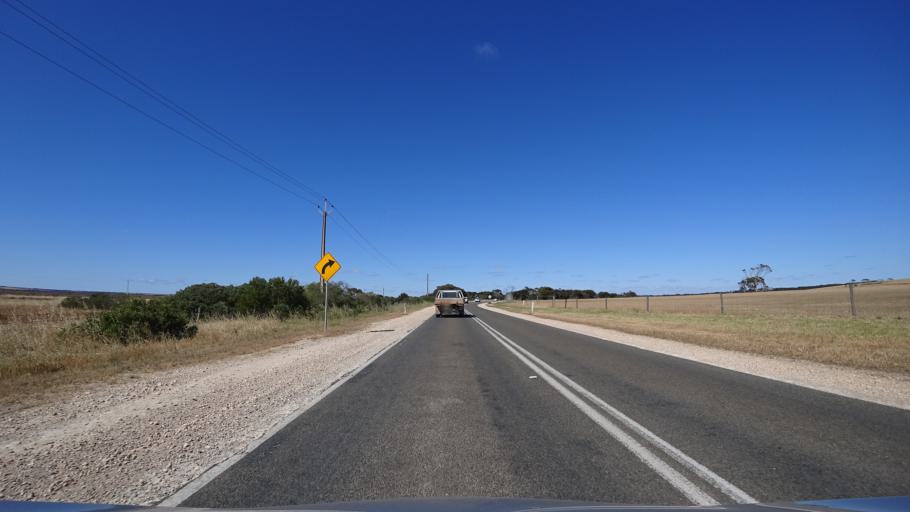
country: AU
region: South Australia
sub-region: Kangaroo Island
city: Kingscote
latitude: -35.6739
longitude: 137.5894
